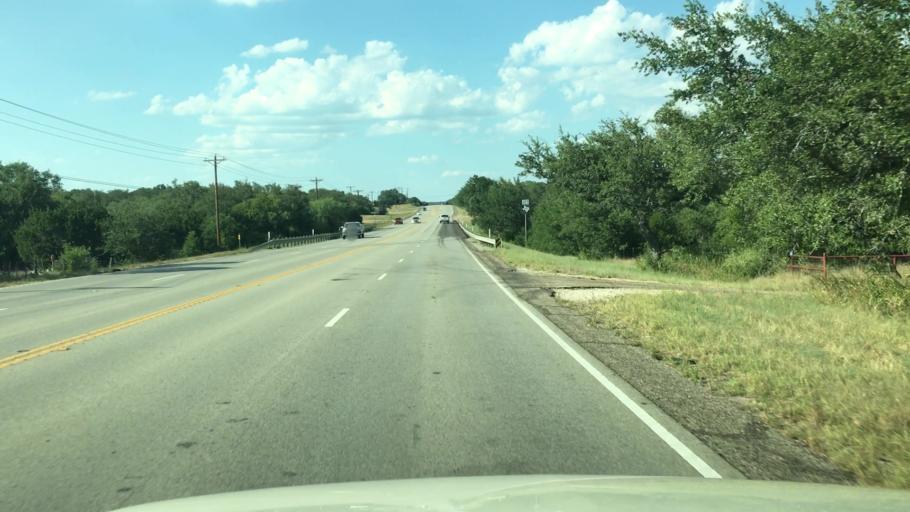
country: US
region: Texas
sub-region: Blanco County
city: Johnson City
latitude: 30.3092
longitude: -98.3936
